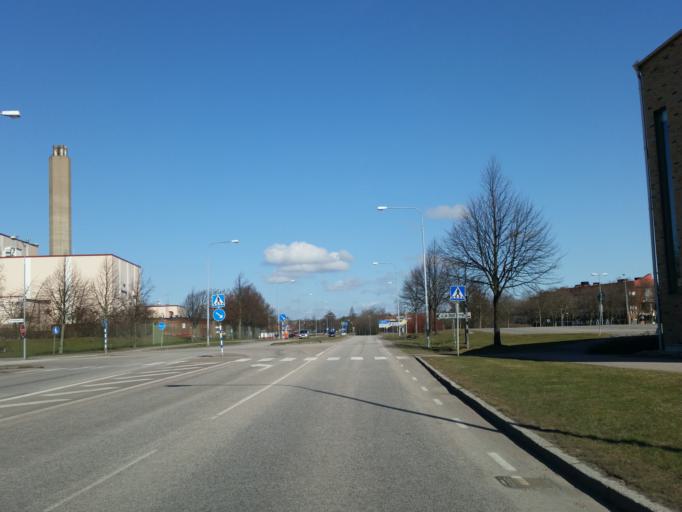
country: SE
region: Kalmar
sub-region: Kalmar Kommun
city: Kalmar
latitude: 56.6666
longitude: 16.3427
